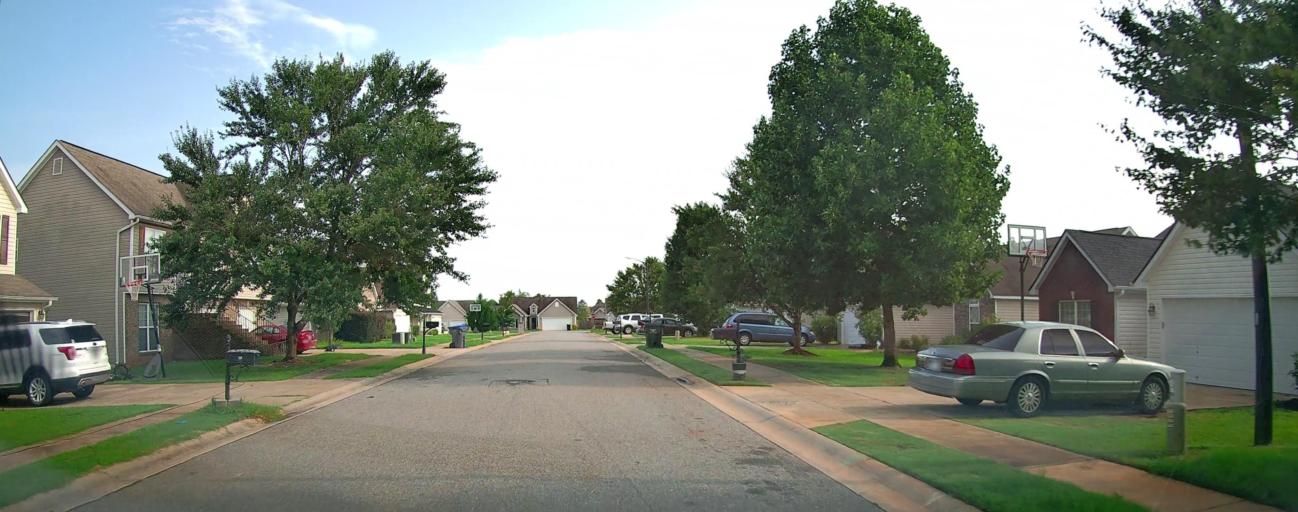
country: US
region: Georgia
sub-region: Houston County
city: Centerville
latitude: 32.6300
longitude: -83.7182
